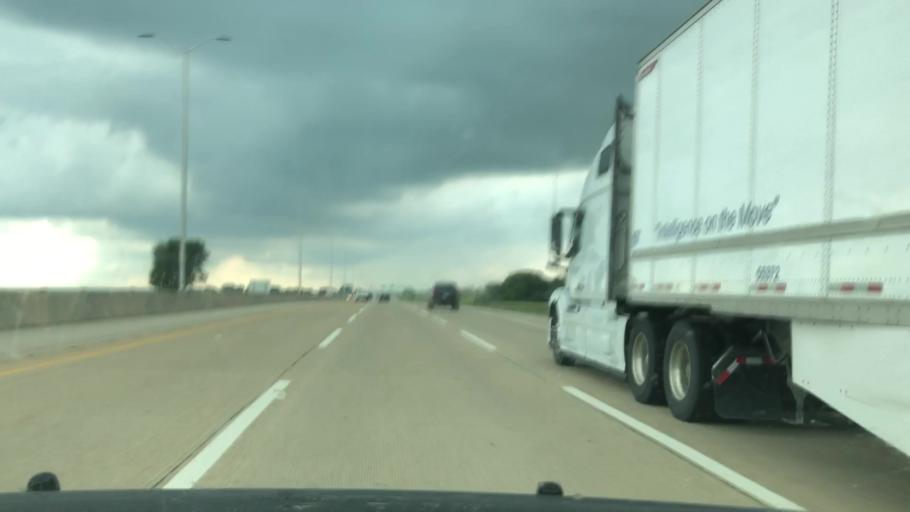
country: US
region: Illinois
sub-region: Boone County
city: Belvidere
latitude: 42.2334
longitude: -88.8840
